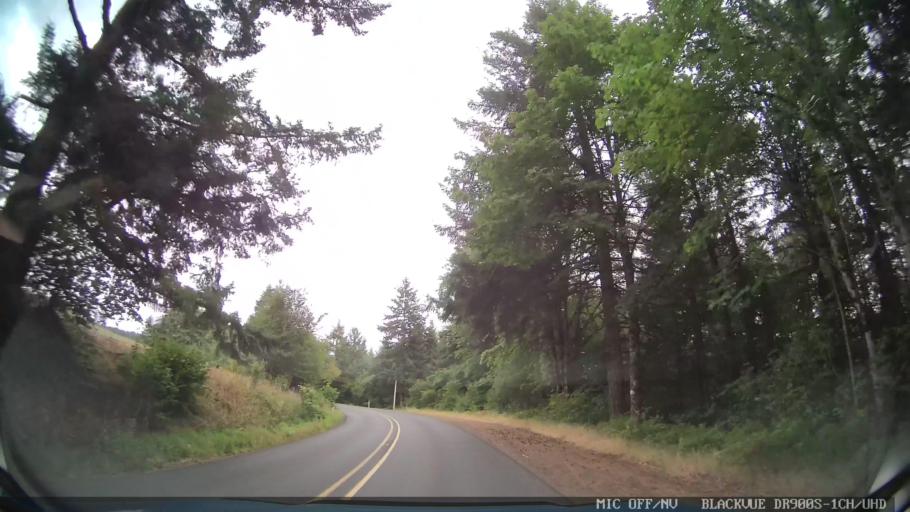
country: US
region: Oregon
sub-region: Linn County
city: Lyons
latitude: 44.8493
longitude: -122.6744
